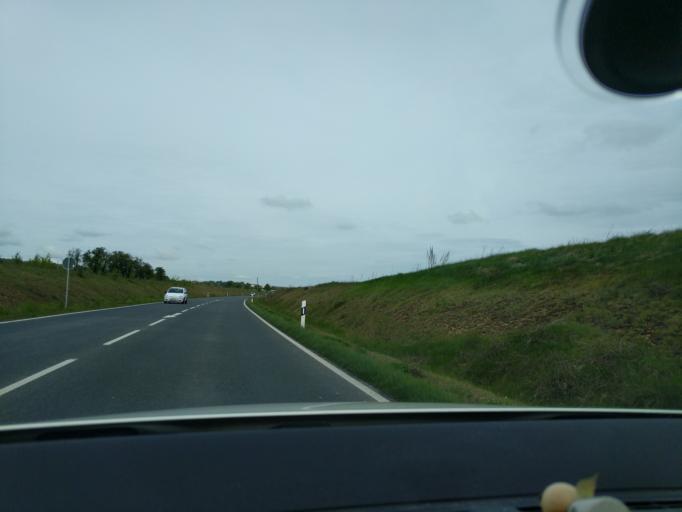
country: DE
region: Saxony
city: Bannewitz
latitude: 50.9875
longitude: 13.7301
